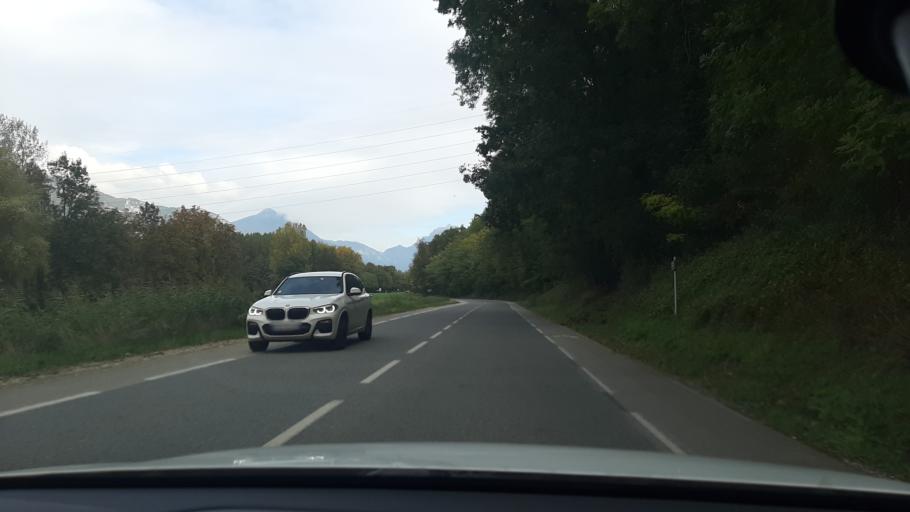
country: FR
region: Rhone-Alpes
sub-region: Departement de l'Isere
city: Pontcharra
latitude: 45.4544
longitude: 6.0467
